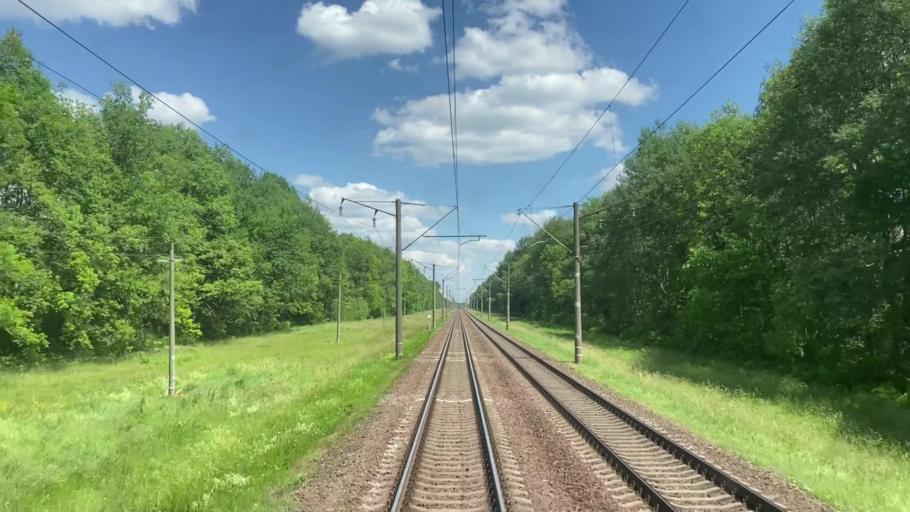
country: BY
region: Brest
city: Pruzhany
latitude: 52.4935
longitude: 24.5972
